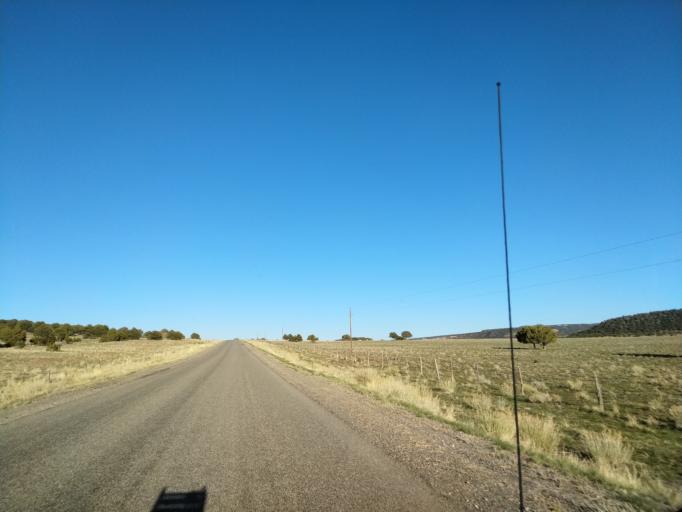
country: US
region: Colorado
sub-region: Mesa County
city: Loma
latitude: 38.9487
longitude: -108.9685
